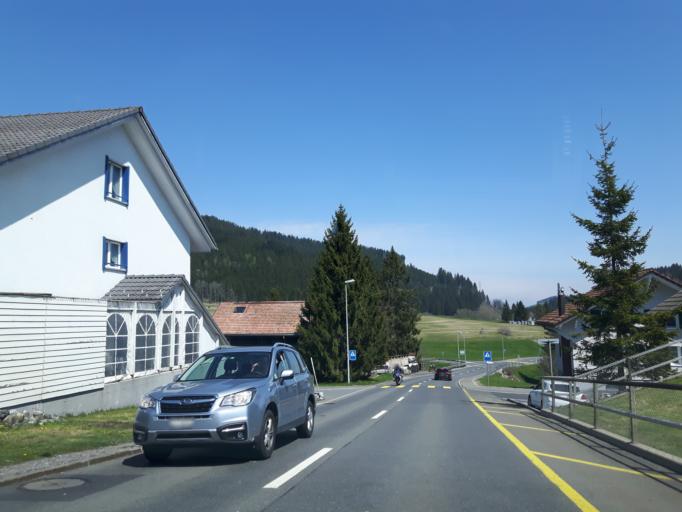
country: CH
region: Schwyz
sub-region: Bezirk Hoefe
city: Schindellegi
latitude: 47.1510
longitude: 8.7165
